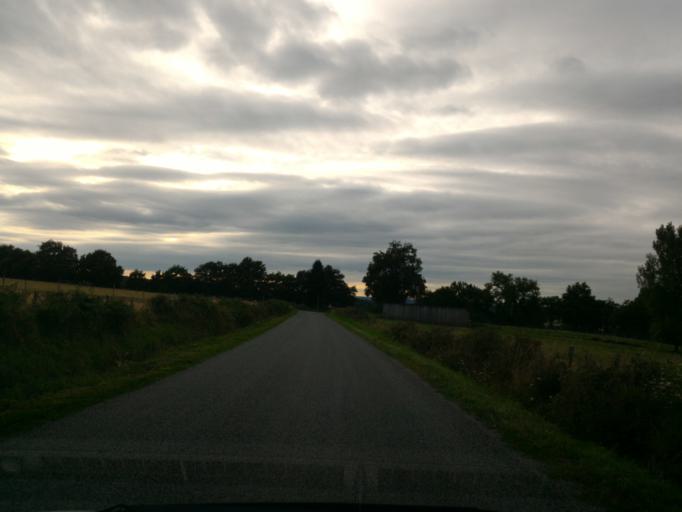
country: FR
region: Poitou-Charentes
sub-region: Departement de la Charente
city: Brigueuil
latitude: 45.9156
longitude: 0.8498
